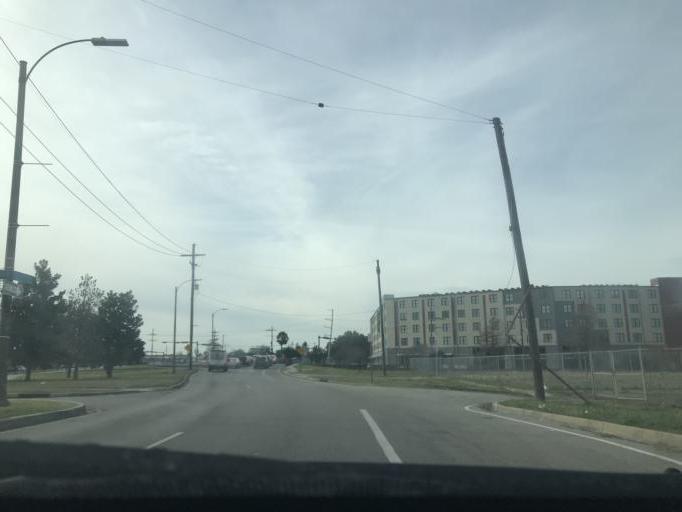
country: US
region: Louisiana
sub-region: Orleans Parish
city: New Orleans
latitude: 29.9593
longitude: -90.1036
